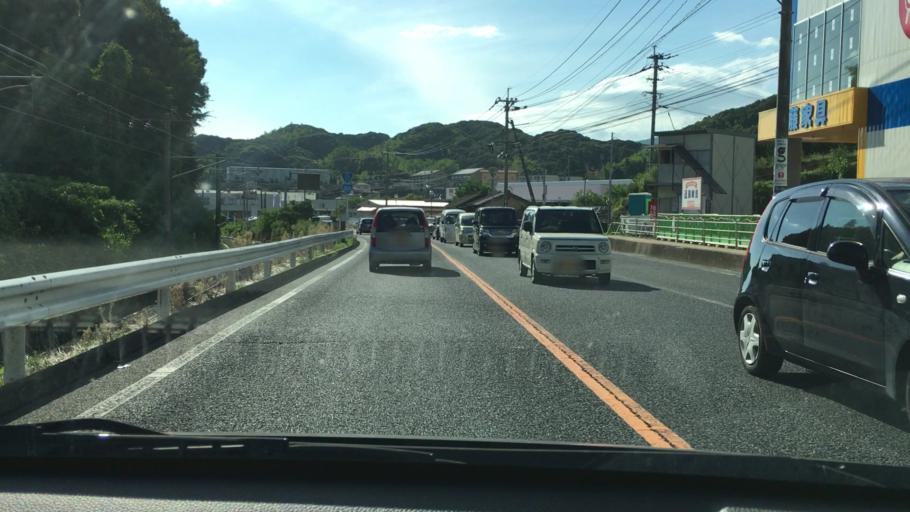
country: JP
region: Nagasaki
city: Sasebo
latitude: 33.1449
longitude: 129.8081
